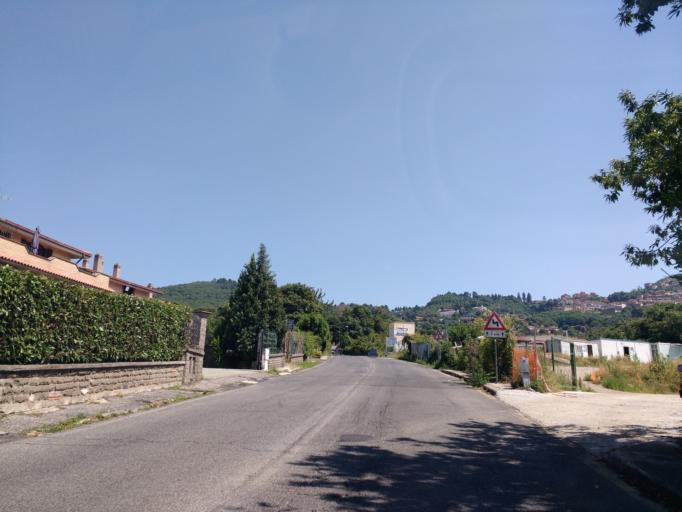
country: IT
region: Latium
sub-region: Citta metropolitana di Roma Capitale
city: Rocca di Papa
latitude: 41.7712
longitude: 12.7030
